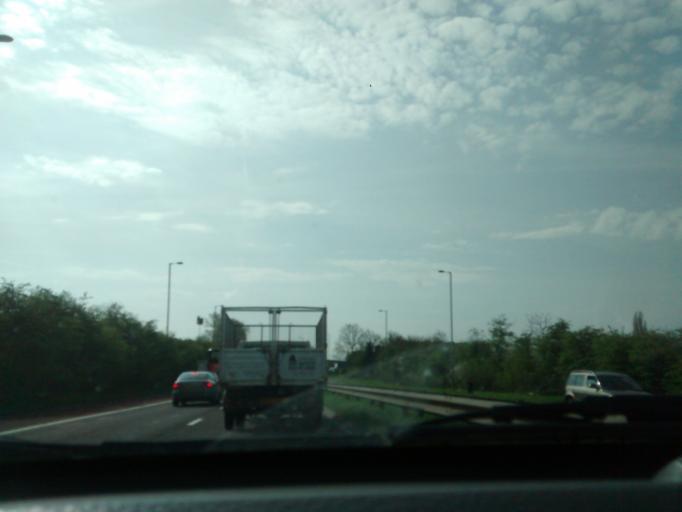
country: GB
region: England
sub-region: Oxfordshire
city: Yarnton
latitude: 51.7914
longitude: -1.2833
